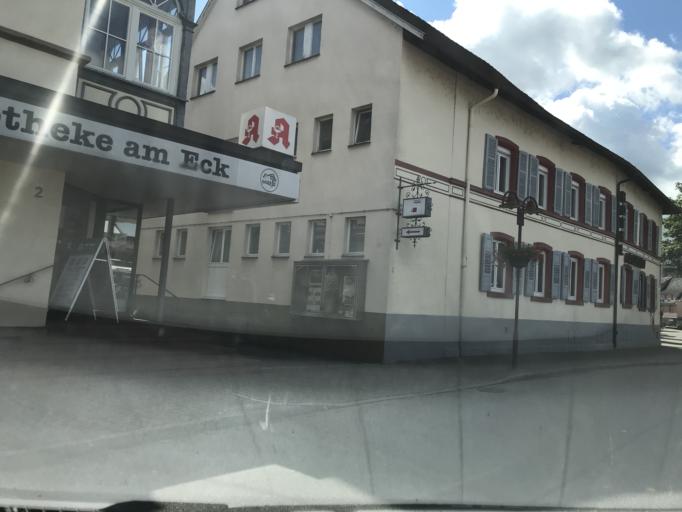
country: DE
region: Baden-Wuerttemberg
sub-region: Freiburg Region
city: Steinen
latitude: 47.6440
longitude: 7.7394
